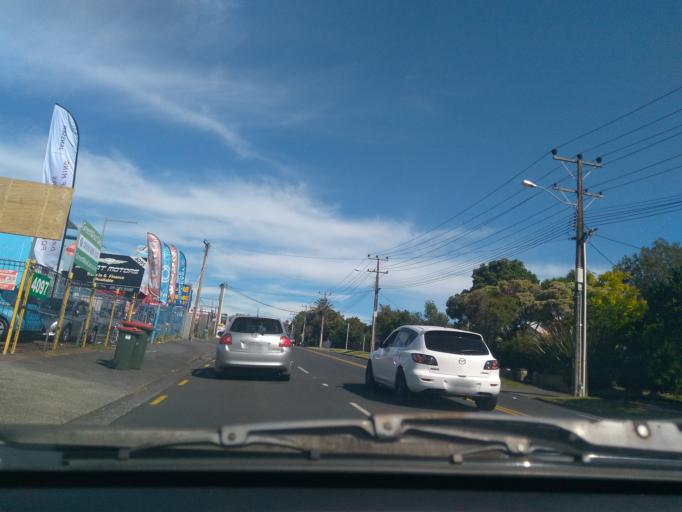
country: NZ
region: Auckland
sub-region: Auckland
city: Waitakere
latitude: -36.9037
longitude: 174.6579
